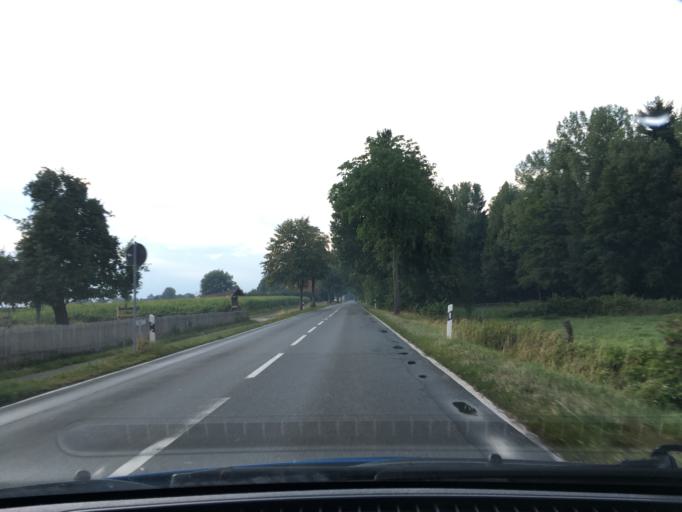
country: DE
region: Lower Saxony
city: Hermannsburg
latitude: 52.7615
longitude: 10.0410
